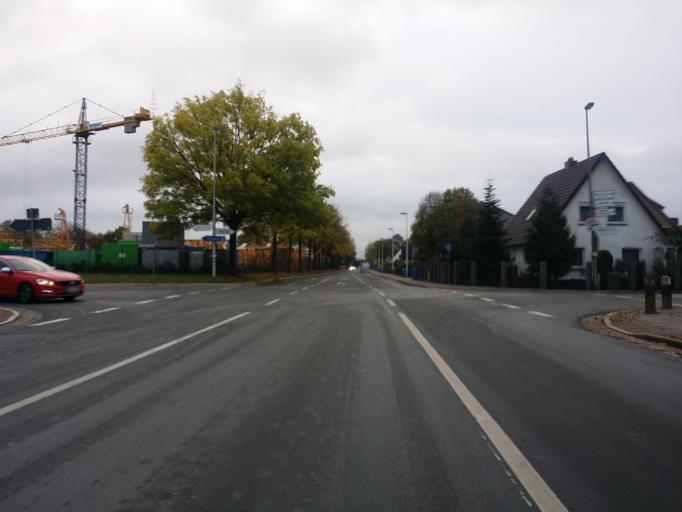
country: DE
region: Lower Saxony
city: Delmenhorst
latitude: 53.0208
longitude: 8.6427
